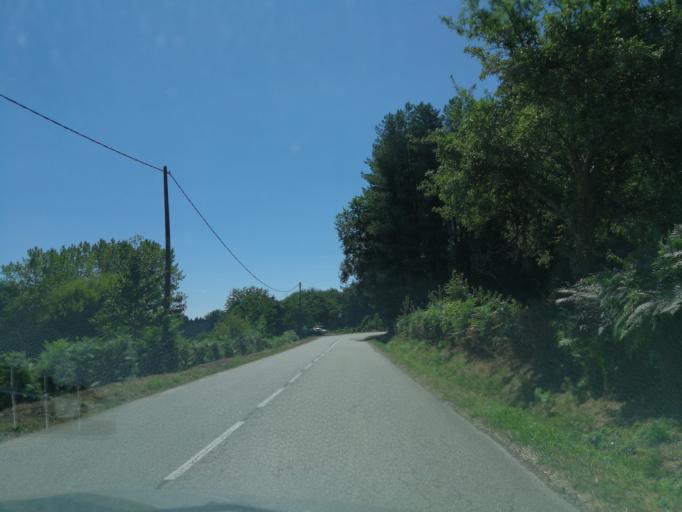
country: FR
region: Limousin
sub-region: Departement de la Correze
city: Argentat
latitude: 45.0357
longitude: 1.9566
